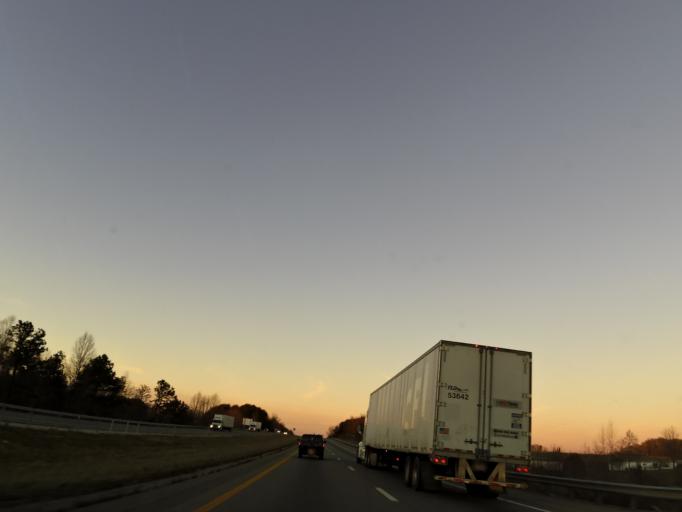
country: US
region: Kentucky
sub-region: Laurel County
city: North Corbin
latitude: 36.9874
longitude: -84.1090
